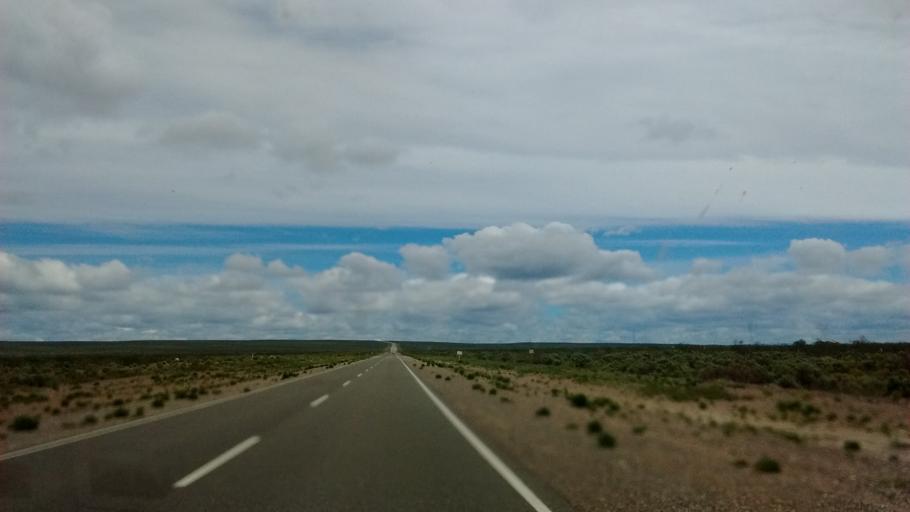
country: AR
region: Neuquen
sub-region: Departamento de Picun Leufu
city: Picun Leufu
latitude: -39.7160
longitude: -69.5278
